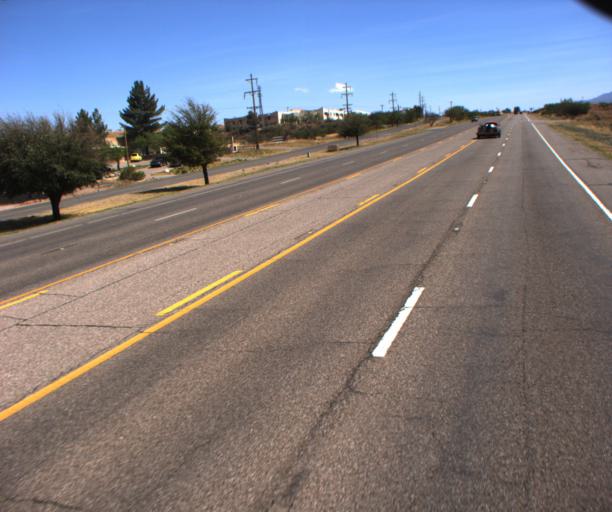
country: US
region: Arizona
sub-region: Cochise County
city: Huachuca City
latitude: 31.6409
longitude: -110.3389
